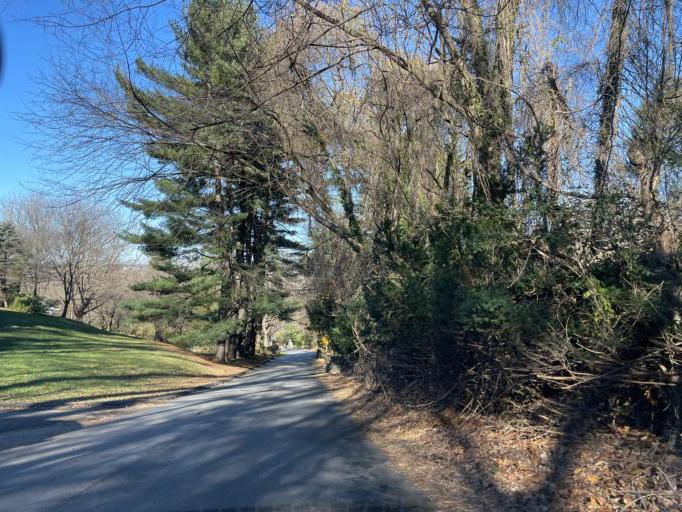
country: US
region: Maryland
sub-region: Baltimore County
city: Mays Chapel
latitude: 39.3994
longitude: -76.6584
